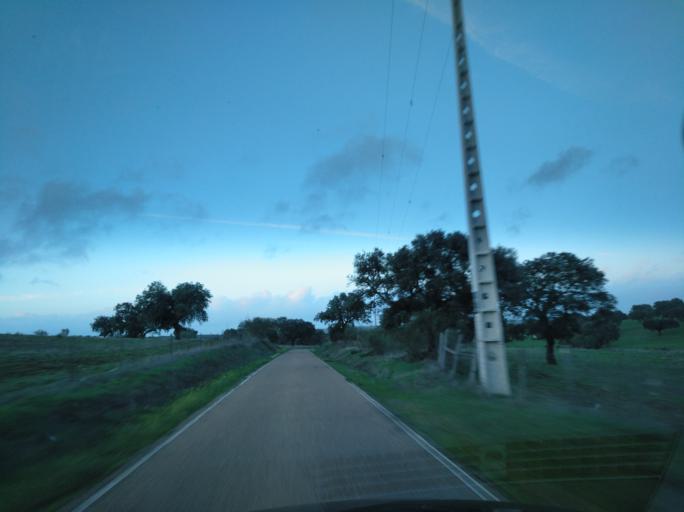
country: PT
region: Portalegre
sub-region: Campo Maior
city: Campo Maior
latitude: 39.0823
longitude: -7.1171
